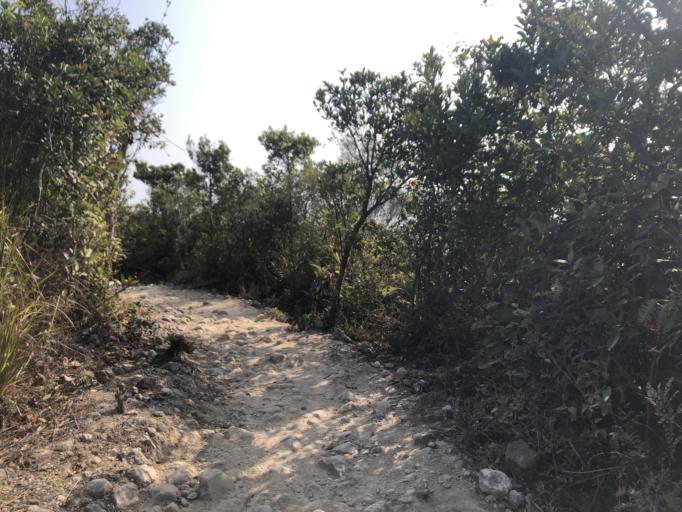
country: HK
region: Sai Kung
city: Sai Kung
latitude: 22.3643
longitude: 114.2921
